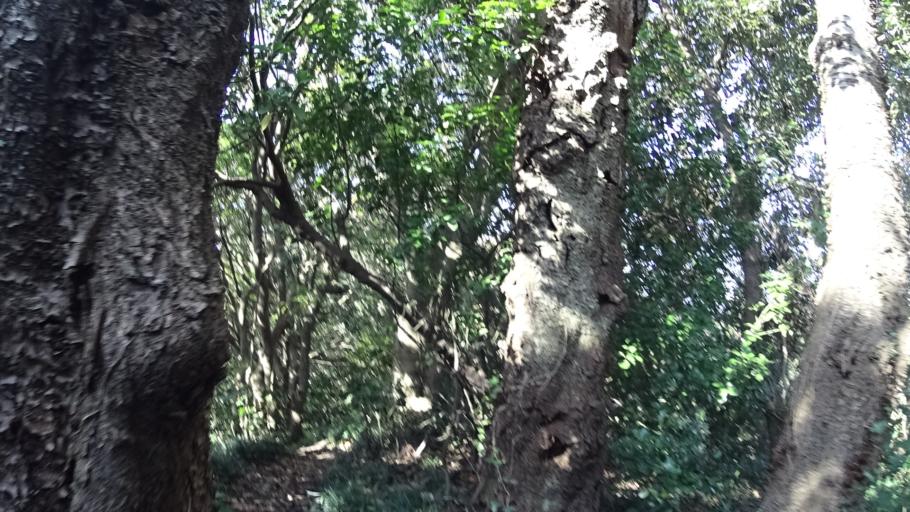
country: JP
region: Kanagawa
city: Hayama
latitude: 35.2764
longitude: 139.6182
